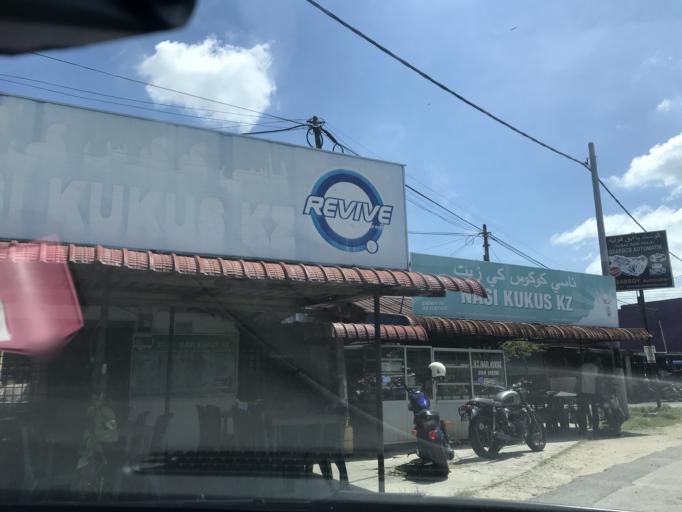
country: MY
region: Kelantan
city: Kota Bharu
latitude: 6.1127
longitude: 102.2650
